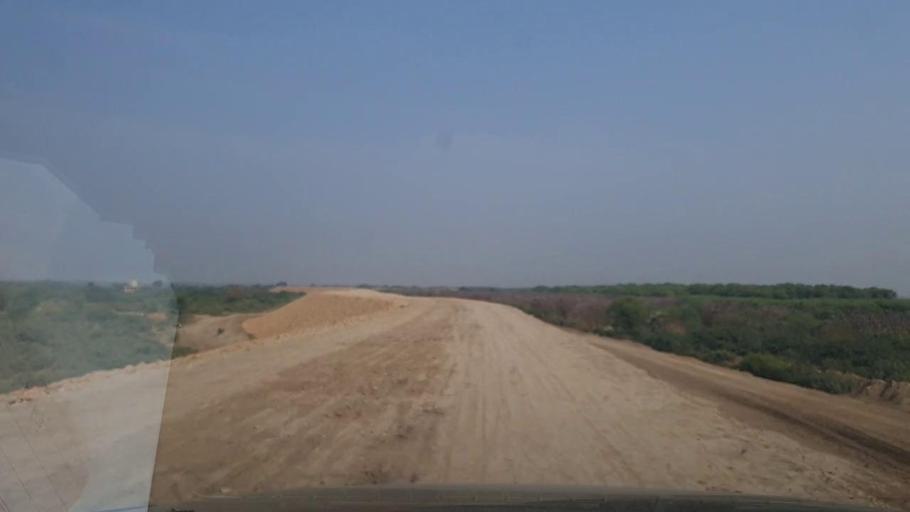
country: PK
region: Sindh
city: Bulri
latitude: 24.9622
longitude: 68.2918
